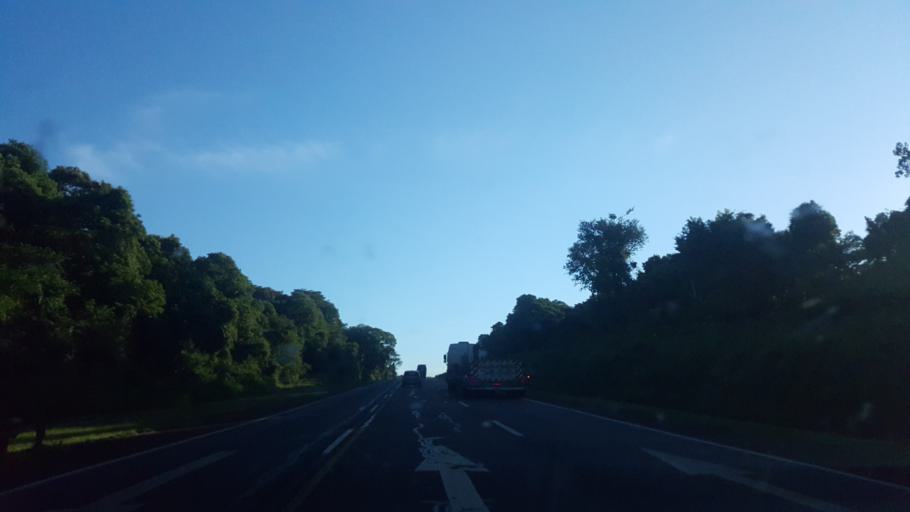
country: AR
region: Misiones
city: El Alcazar
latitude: -26.7125
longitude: -54.8497
